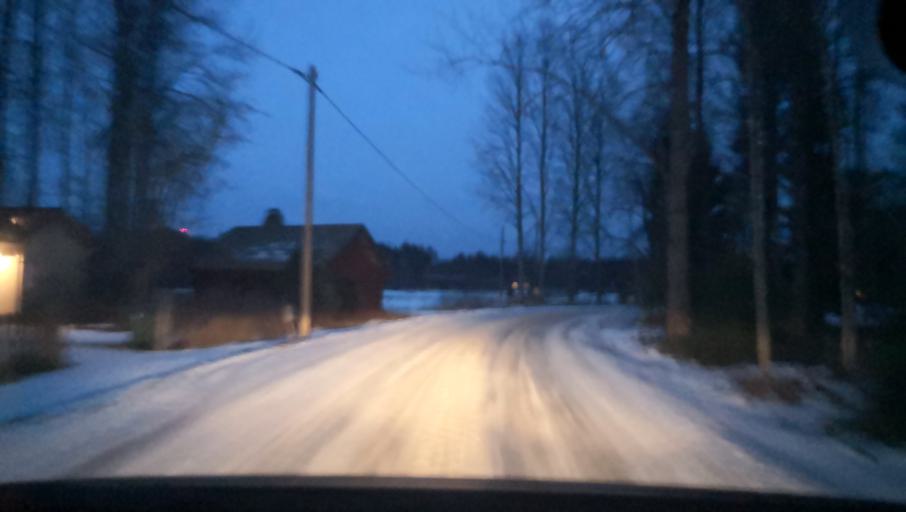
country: SE
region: Uppsala
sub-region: Heby Kommun
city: Tarnsjo
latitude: 60.2427
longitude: 16.6950
